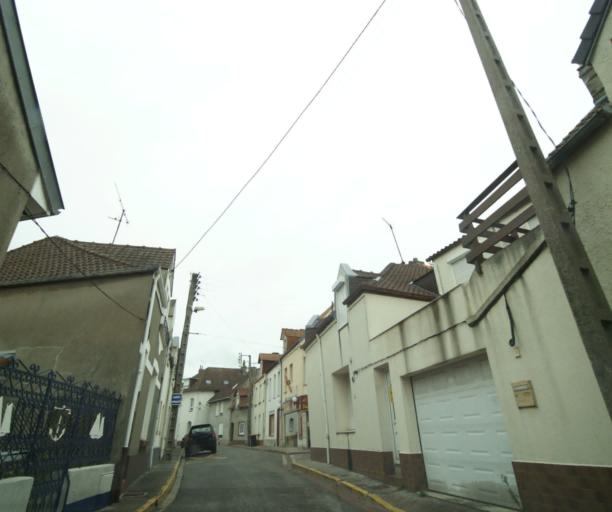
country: FR
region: Nord-Pas-de-Calais
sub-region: Departement du Pas-de-Calais
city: Etaples
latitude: 50.5159
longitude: 1.6388
